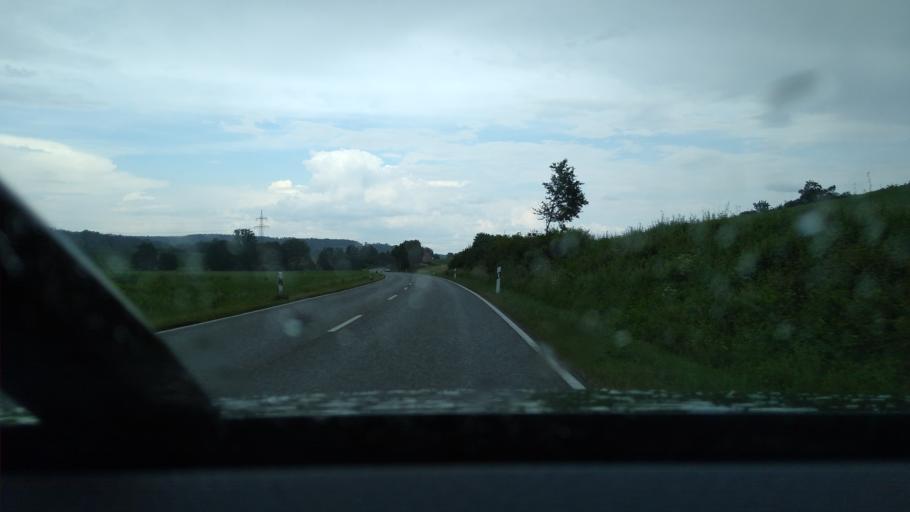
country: DE
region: Bavaria
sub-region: Regierungsbezirk Mittelfranken
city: Obernzenn
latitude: 49.4512
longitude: 10.4772
